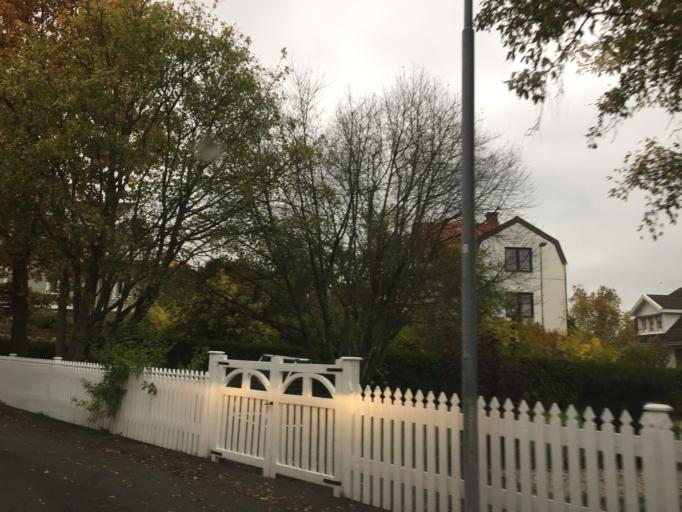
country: SE
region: Vaestra Goetaland
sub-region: Trollhattan
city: Trollhattan
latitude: 58.2854
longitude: 12.2760
